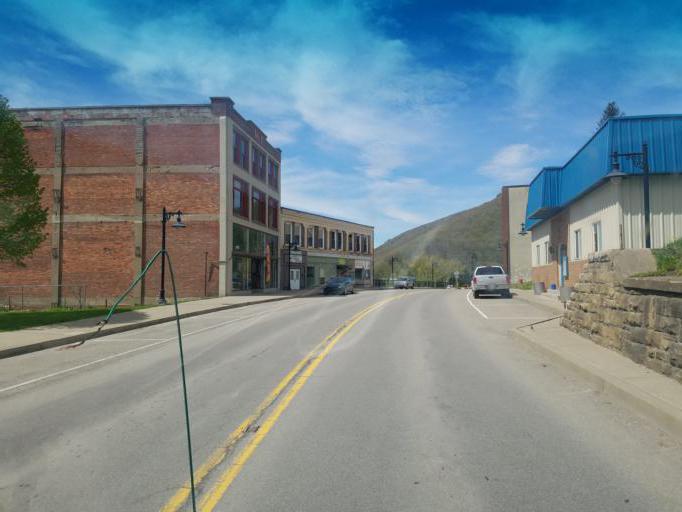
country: US
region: Pennsylvania
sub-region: Potter County
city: Galeton
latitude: 41.7356
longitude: -77.6433
